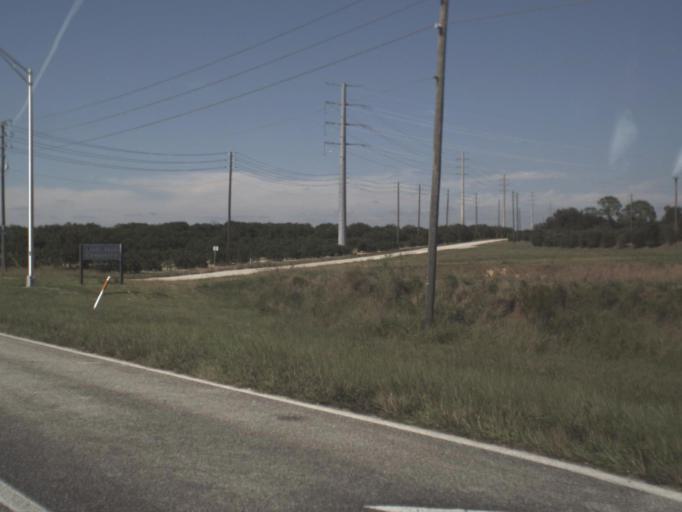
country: US
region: Florida
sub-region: Highlands County
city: Lake Placid
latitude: 27.3205
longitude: -81.3670
